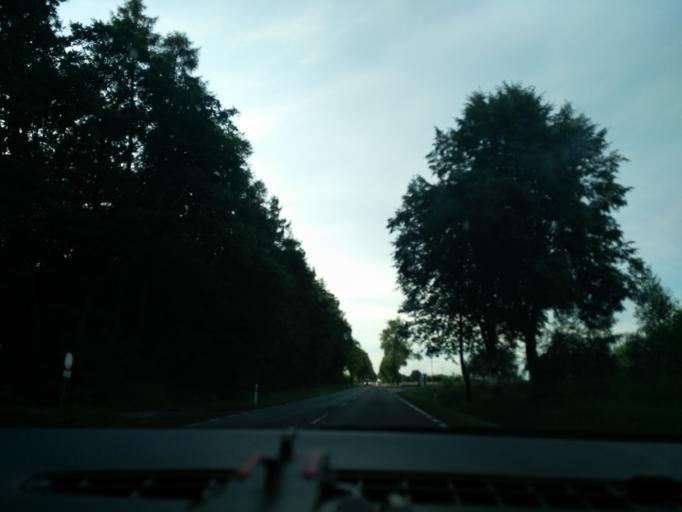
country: PL
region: Lublin Voivodeship
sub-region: Powiat krasnicki
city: Szastarka
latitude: 50.8711
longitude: 22.2707
